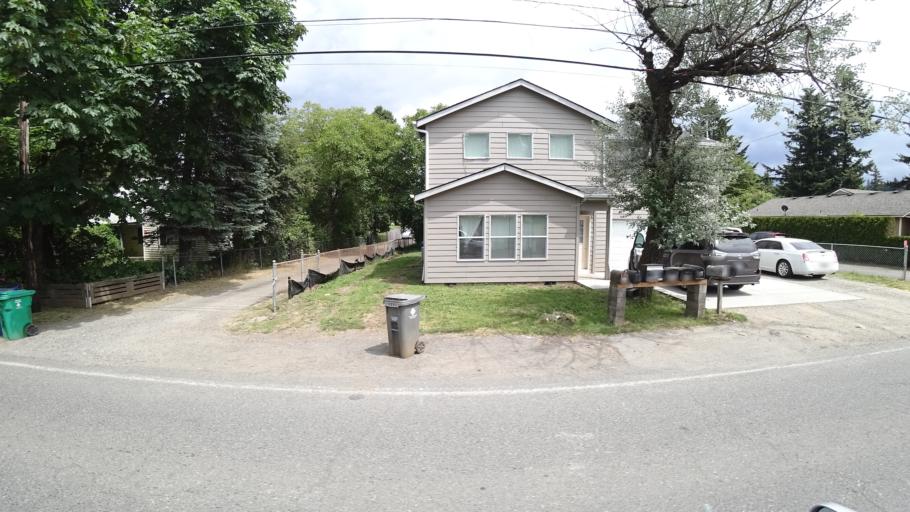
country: US
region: Oregon
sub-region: Clackamas County
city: Happy Valley
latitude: 45.5005
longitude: -122.5138
